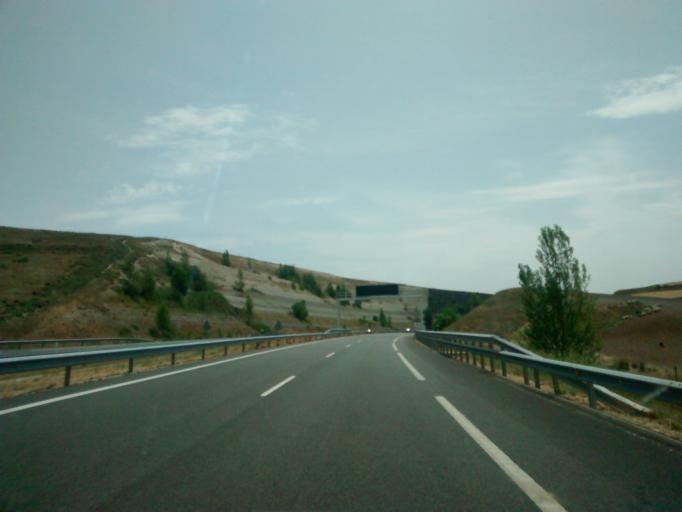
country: ES
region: Castille and Leon
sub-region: Provincia de Burgos
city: Tardajos
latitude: 42.3594
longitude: -3.8048
